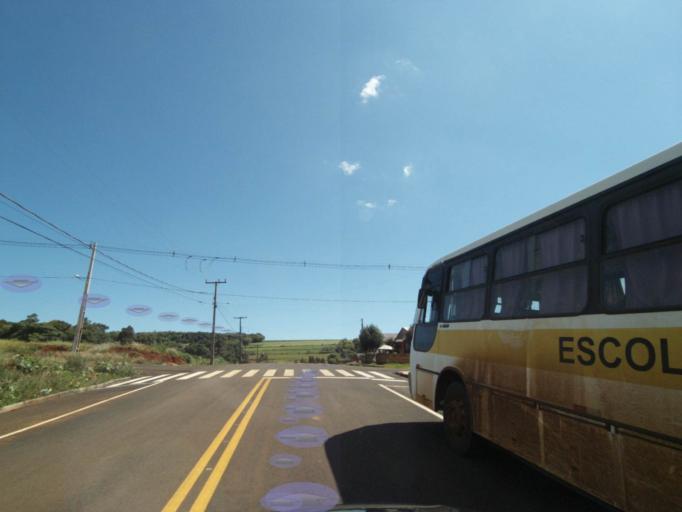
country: BR
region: Parana
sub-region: Coronel Vivida
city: Coronel Vivida
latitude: -26.1468
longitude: -52.3824
